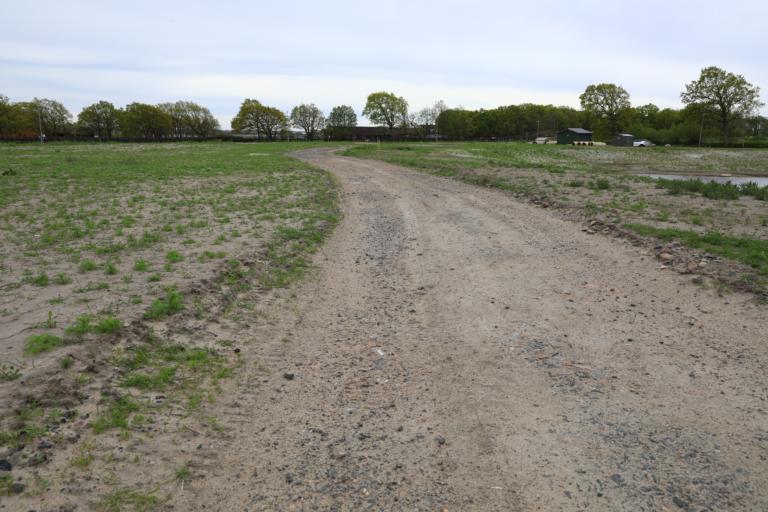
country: SE
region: Halland
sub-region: Varbergs Kommun
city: Varberg
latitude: 57.1455
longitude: 12.2377
